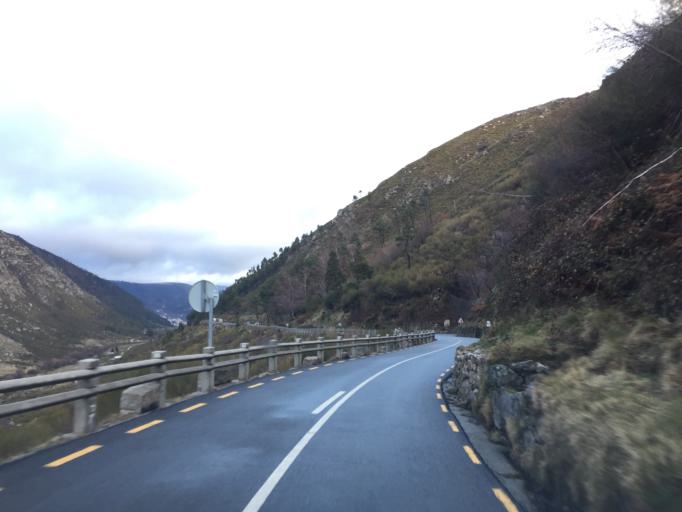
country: PT
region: Guarda
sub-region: Manteigas
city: Manteigas
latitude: 40.3435
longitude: -7.5635
